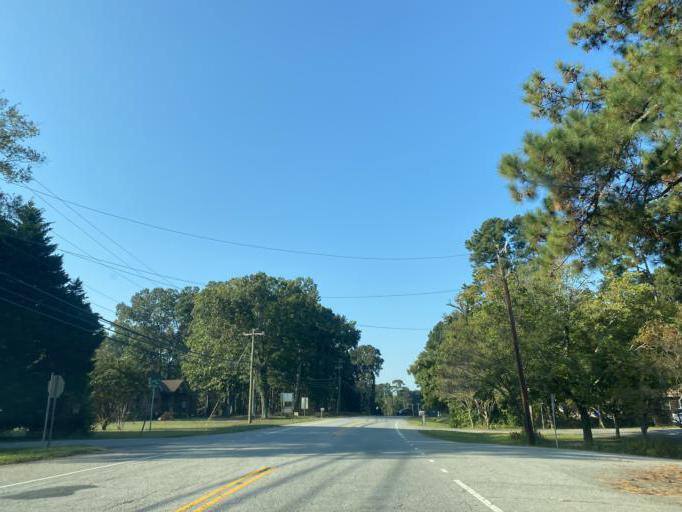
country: US
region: South Carolina
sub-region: Cherokee County
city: Gaffney
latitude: 35.0559
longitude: -81.6641
